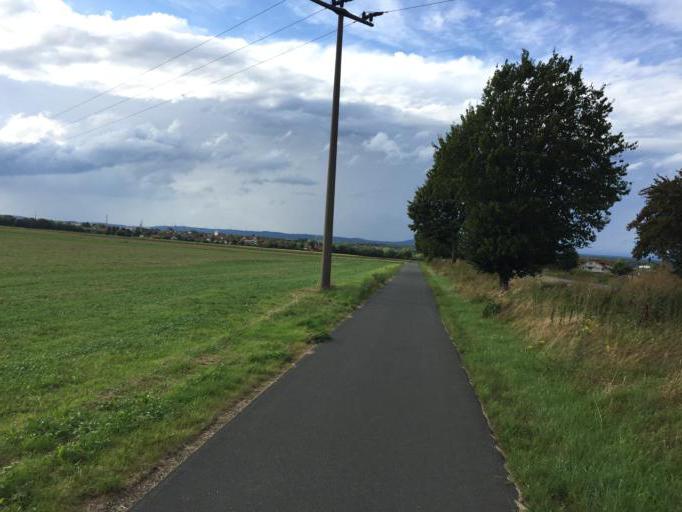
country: DE
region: Hesse
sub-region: Regierungsbezirk Giessen
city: Langgons
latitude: 50.5173
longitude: 8.6768
